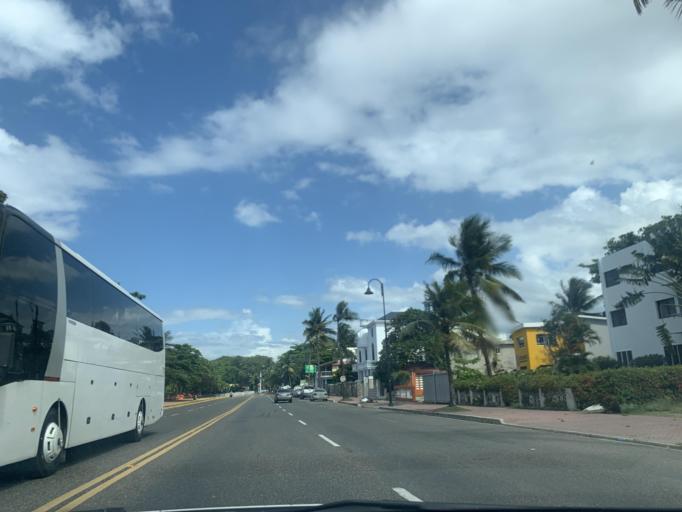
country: DO
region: Puerto Plata
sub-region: Puerto Plata
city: Puerto Plata
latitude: 19.7937
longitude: -70.6793
